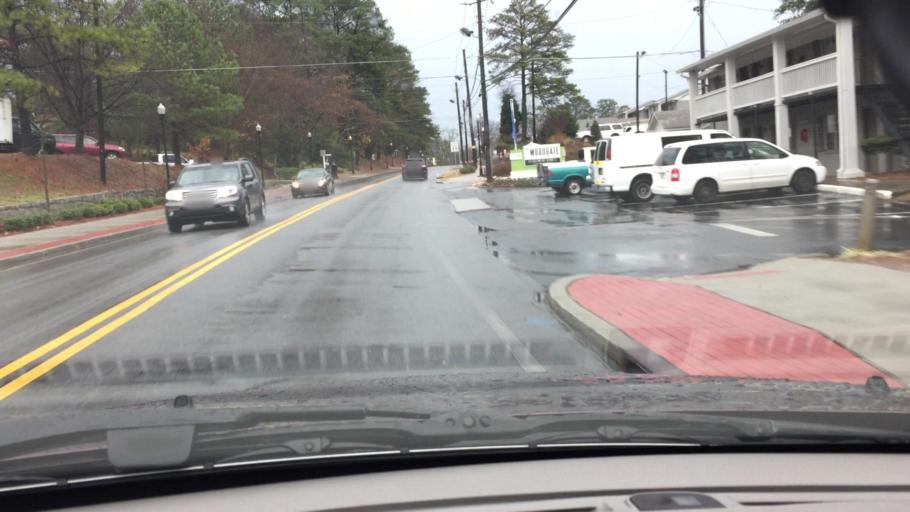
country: US
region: Georgia
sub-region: DeKalb County
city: Chamblee
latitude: 33.8913
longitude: -84.2909
